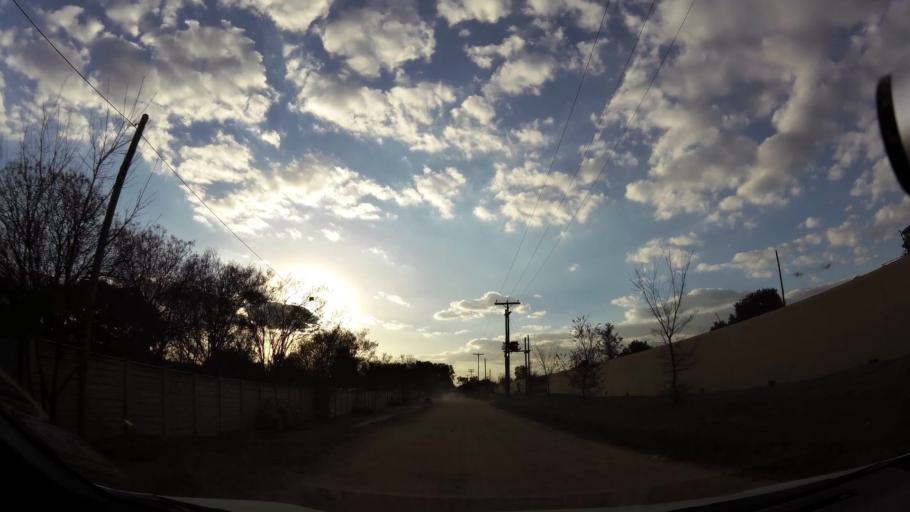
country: ZA
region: Gauteng
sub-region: City of Johannesburg Metropolitan Municipality
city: Diepsloot
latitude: -26.0047
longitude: 27.9700
